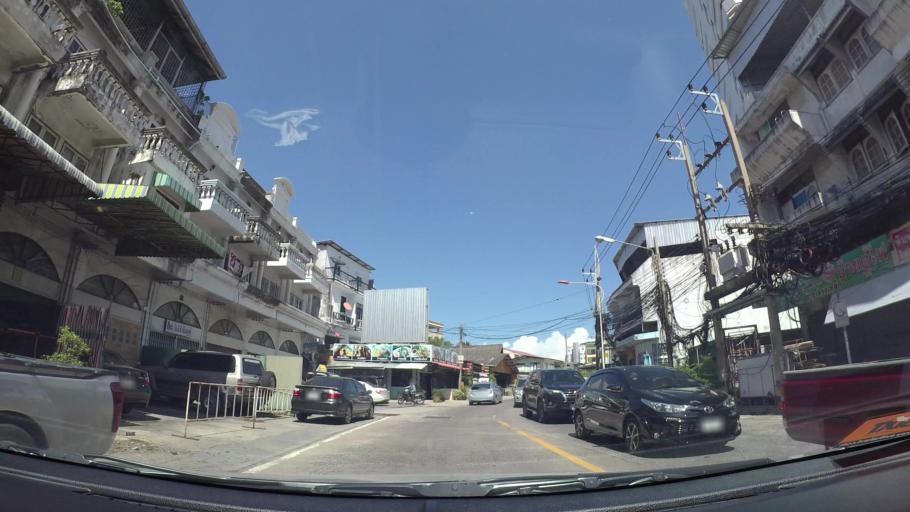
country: TH
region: Chon Buri
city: Si Racha
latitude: 13.1628
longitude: 100.9296
